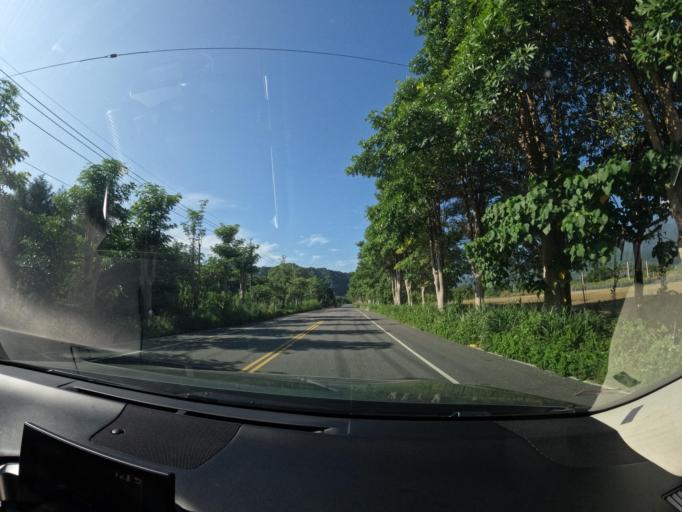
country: TW
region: Taiwan
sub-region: Hualien
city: Hualian
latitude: 23.4885
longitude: 121.3750
